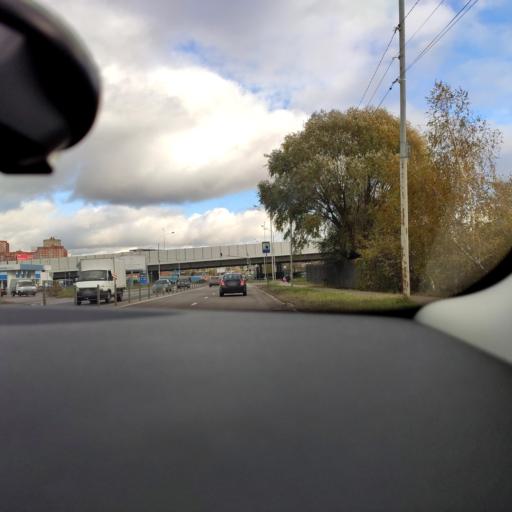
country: RU
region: Moskovskaya
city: Kotel'niki
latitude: 55.6523
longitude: 37.8515
